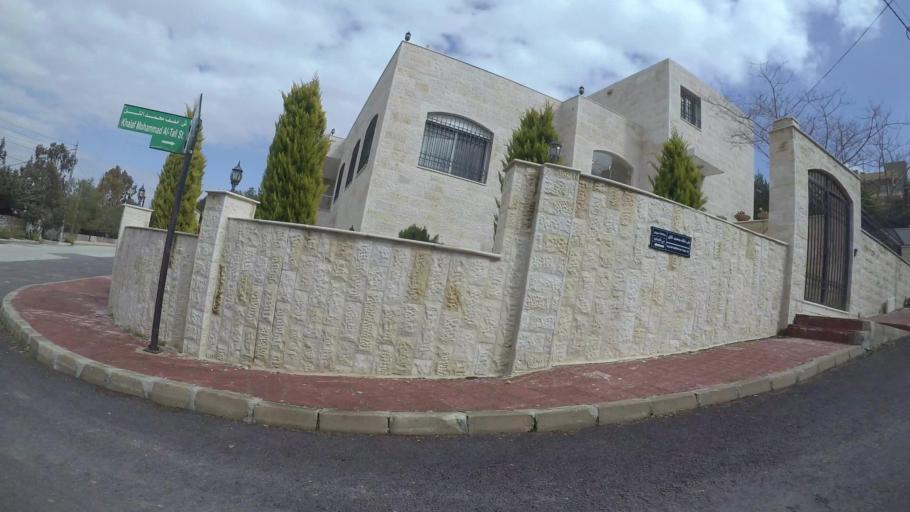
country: JO
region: Amman
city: Al Jubayhah
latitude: 32.0349
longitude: 35.8155
